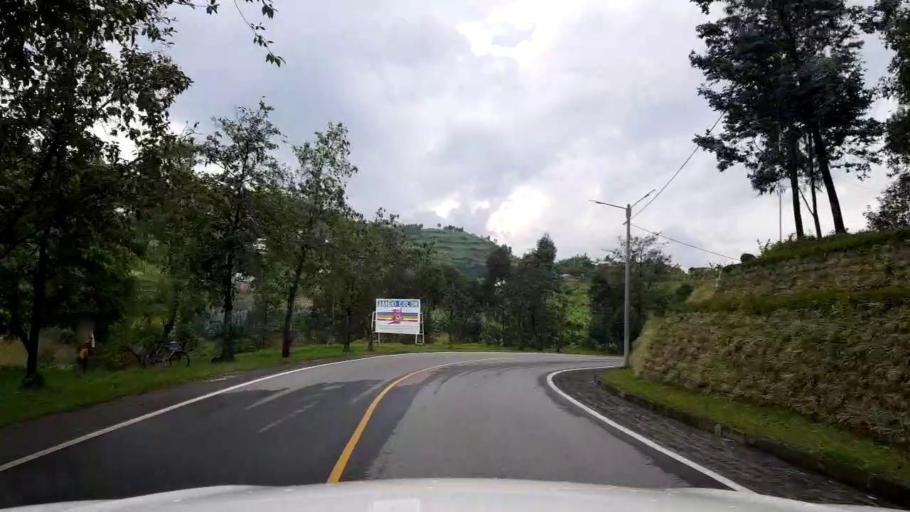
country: RW
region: Western Province
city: Gisenyi
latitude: -1.7011
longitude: 29.2716
